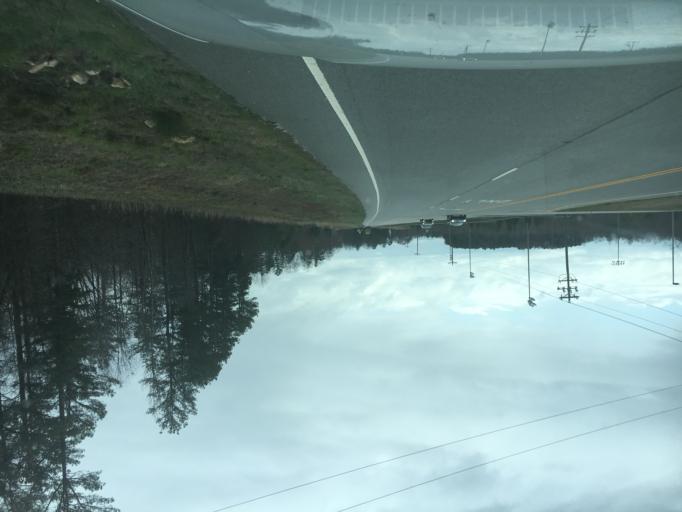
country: US
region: South Carolina
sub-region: Oconee County
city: Walhalla
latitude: 34.8194
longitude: -83.0403
